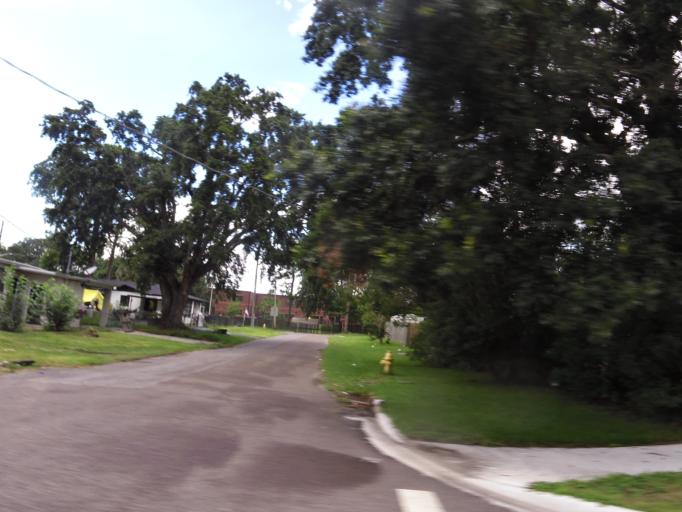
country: US
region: Florida
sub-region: Duval County
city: Jacksonville
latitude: 30.3727
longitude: -81.6547
